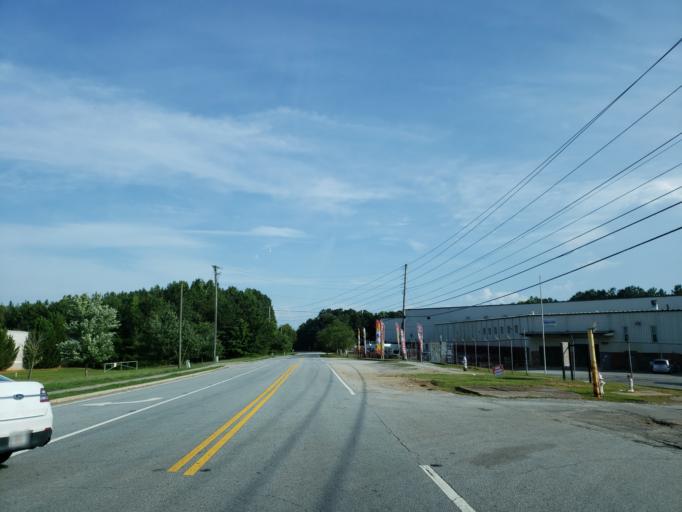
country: US
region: Georgia
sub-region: Cobb County
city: Powder Springs
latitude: 33.8736
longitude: -84.7030
